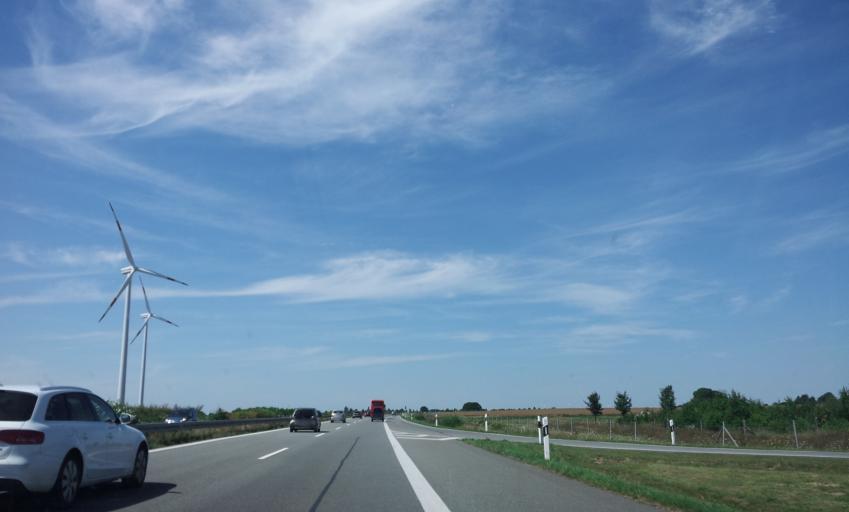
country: DE
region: Mecklenburg-Vorpommern
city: Gormin
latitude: 53.9976
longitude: 13.3177
